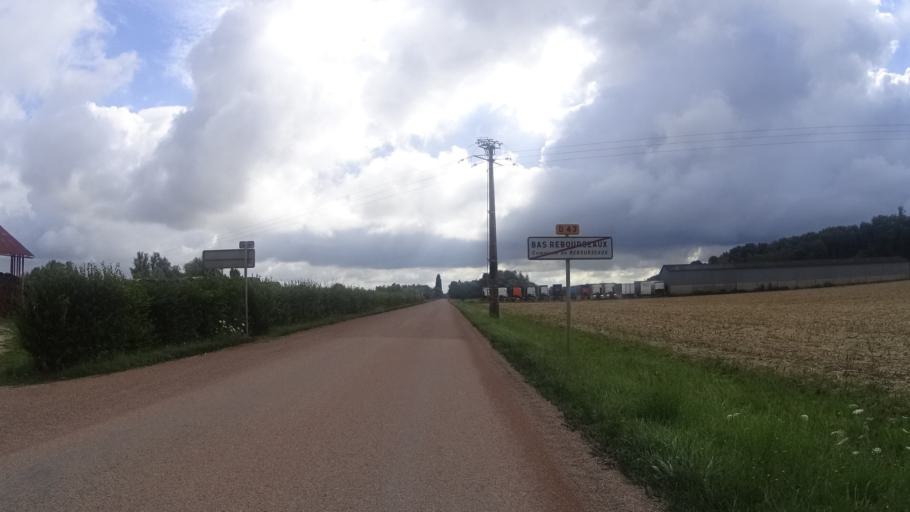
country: FR
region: Bourgogne
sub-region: Departement de l'Yonne
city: Vergigny
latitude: 47.9660
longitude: 3.6878
